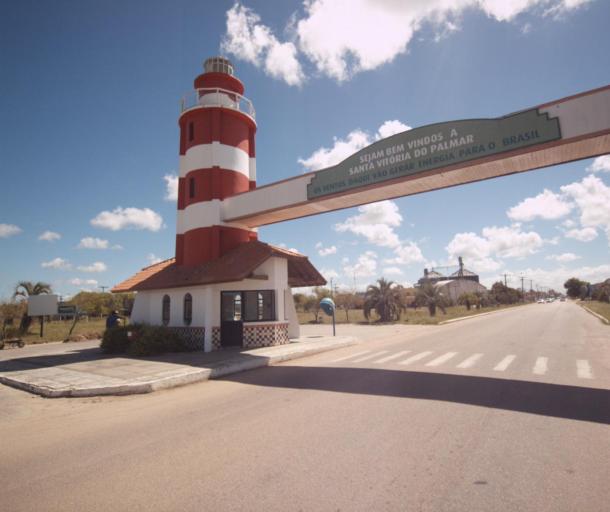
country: BR
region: Rio Grande do Sul
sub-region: Santa Vitoria Do Palmar
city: Santa Vitoria do Palmar
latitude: -33.5304
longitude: -53.3462
